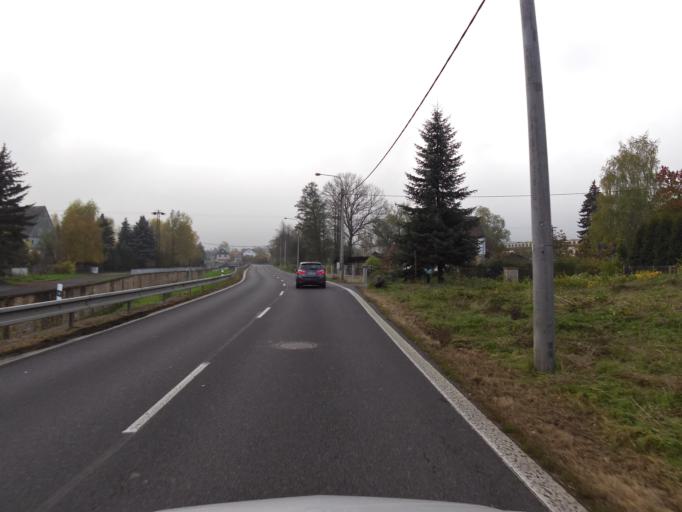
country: CZ
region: Ustecky
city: Libouchec
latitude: 50.7598
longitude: 14.0656
